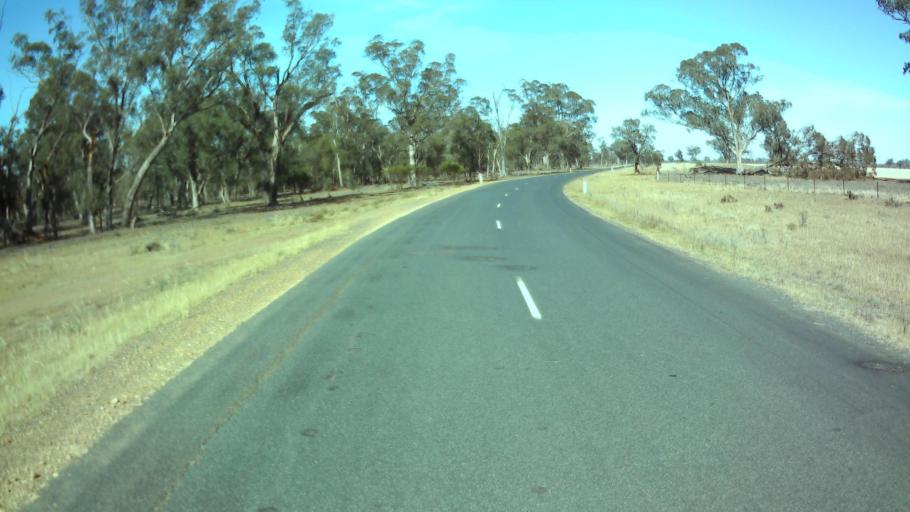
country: AU
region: New South Wales
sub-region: Weddin
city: Grenfell
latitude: -34.1352
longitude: 147.7885
